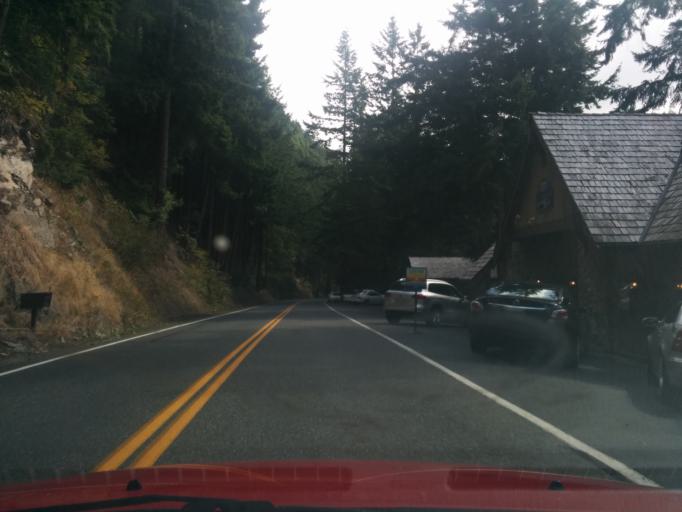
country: US
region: Washington
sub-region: Whatcom County
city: Geneva
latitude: 48.6106
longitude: -122.4352
